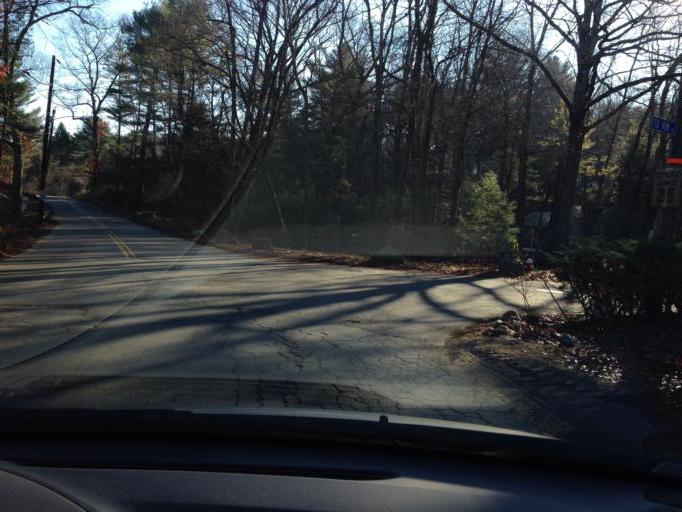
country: US
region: Massachusetts
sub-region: Middlesex County
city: Billerica
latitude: 42.5265
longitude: -71.2811
